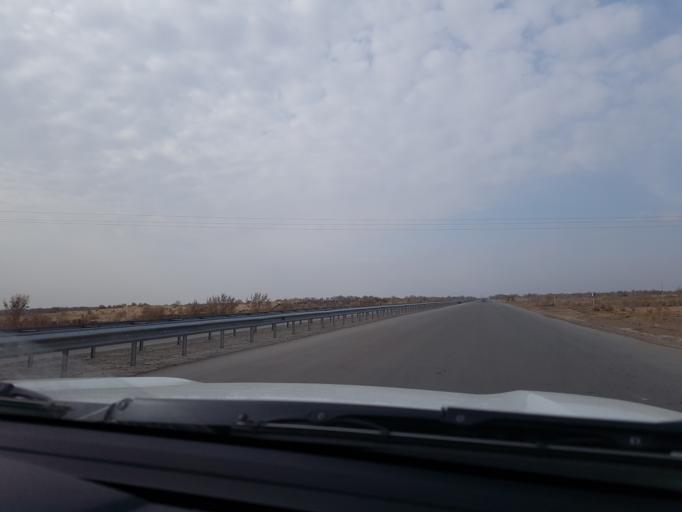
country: TM
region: Dasoguz
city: Yylanly
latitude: 41.7728
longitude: 59.4506
